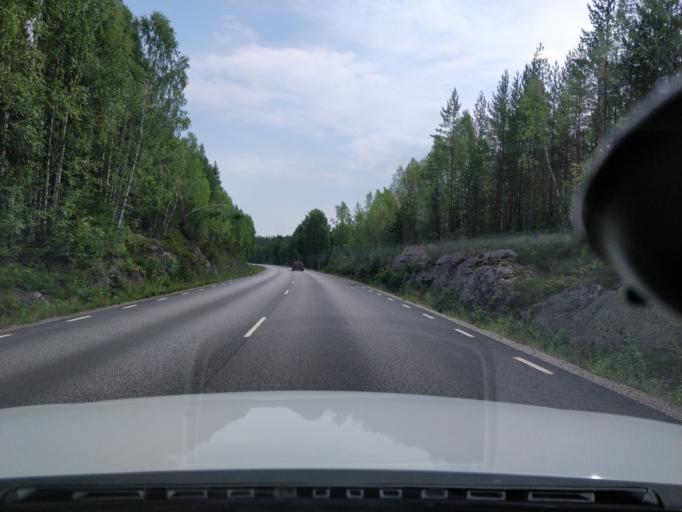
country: SE
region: Dalarna
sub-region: Ludvika Kommun
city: Ludvika
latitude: 60.2910
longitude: 15.2360
